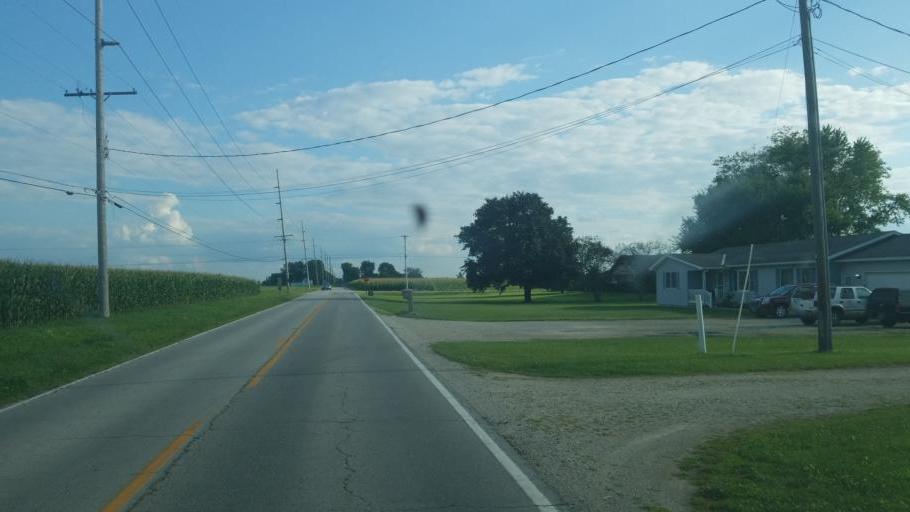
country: US
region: Ohio
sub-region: Sandusky County
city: Ballville
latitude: 41.2928
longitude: -83.1302
